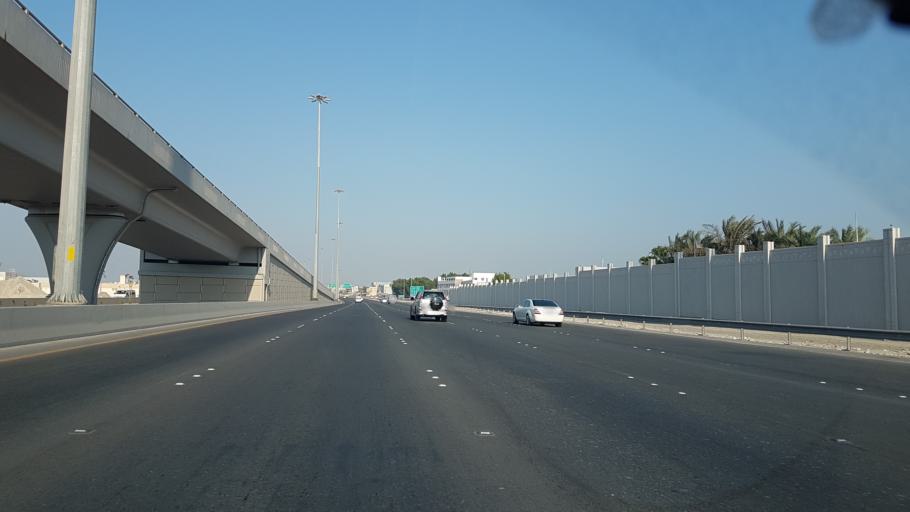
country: BH
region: Northern
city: Ar Rifa'
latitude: 26.1245
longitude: 50.5929
